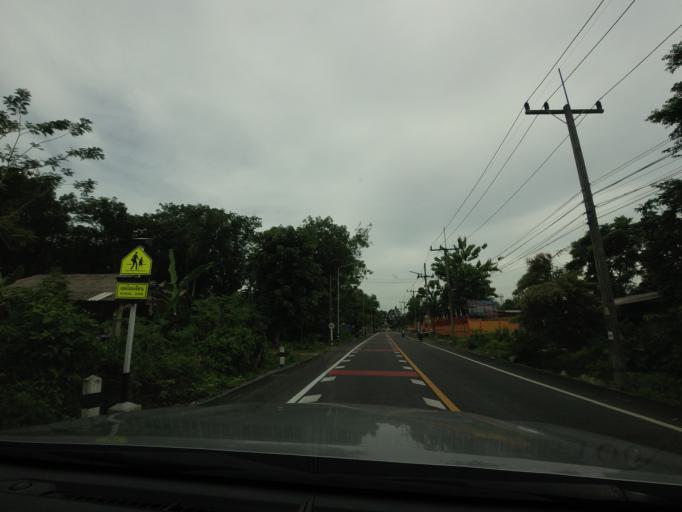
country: TH
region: Yala
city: Raman
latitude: 6.4462
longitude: 101.4513
